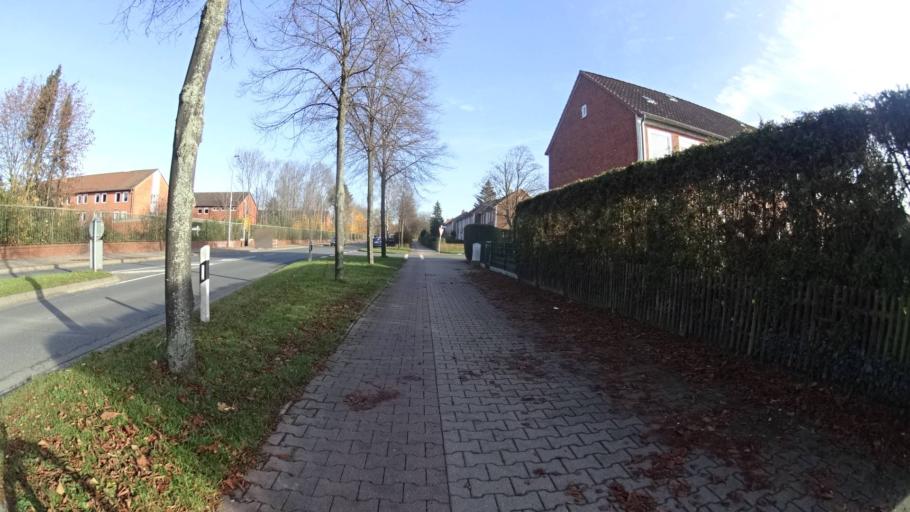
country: DE
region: Lower Saxony
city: Lueneburg
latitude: 53.2507
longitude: 10.4406
